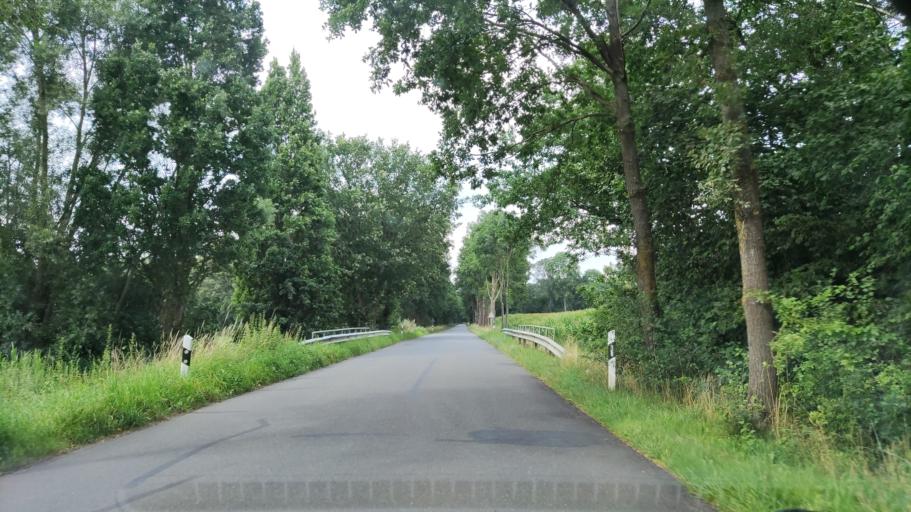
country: DE
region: Lower Saxony
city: Dannenberg
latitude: 53.0890
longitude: 11.1282
